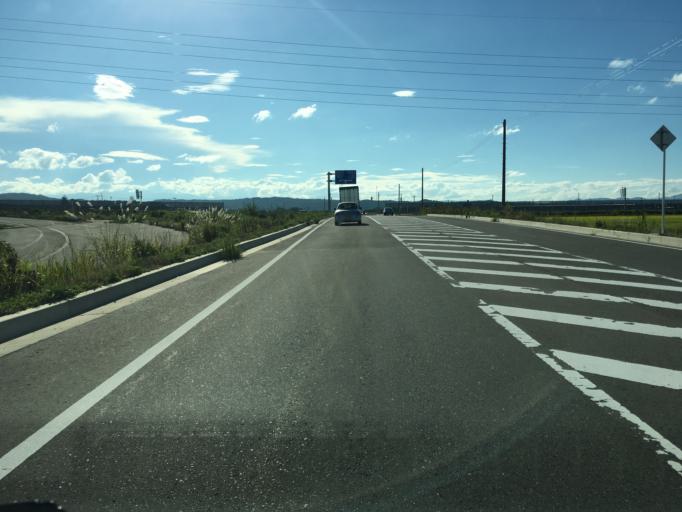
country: JP
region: Yamagata
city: Yonezawa
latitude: 37.9507
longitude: 140.1146
